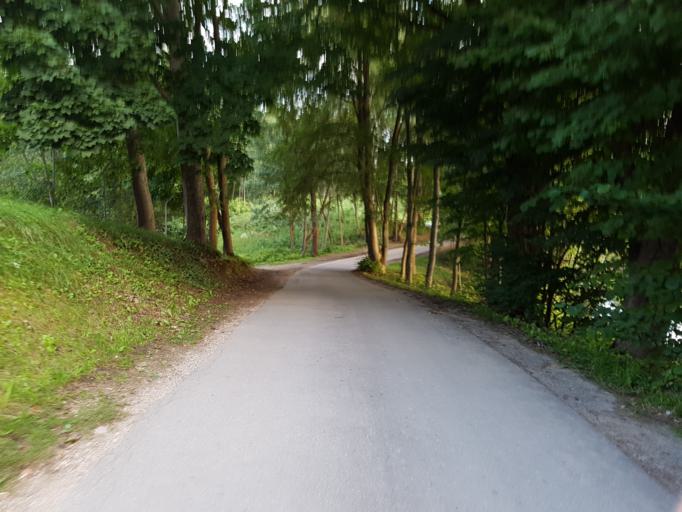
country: LT
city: Trakai
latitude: 54.6691
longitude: 24.9294
